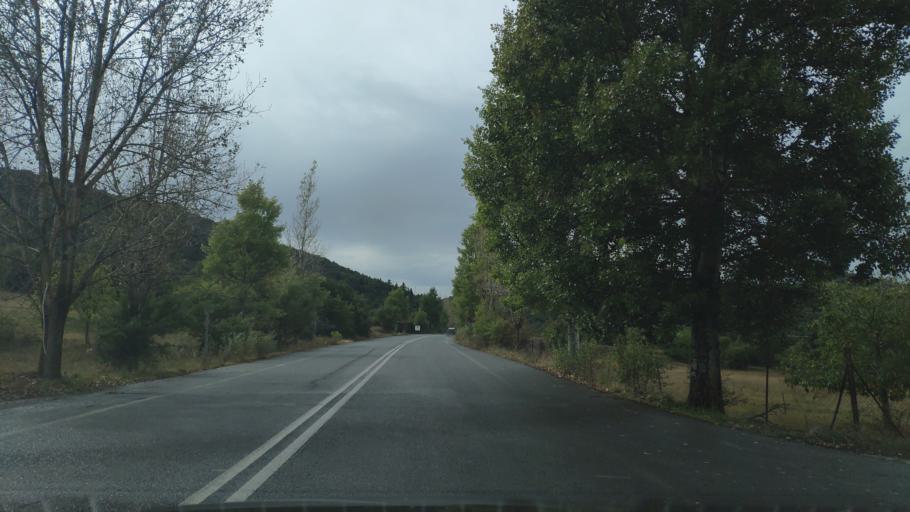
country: GR
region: Peloponnese
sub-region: Nomos Arkadias
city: Langadhia
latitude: 37.6893
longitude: 22.1948
